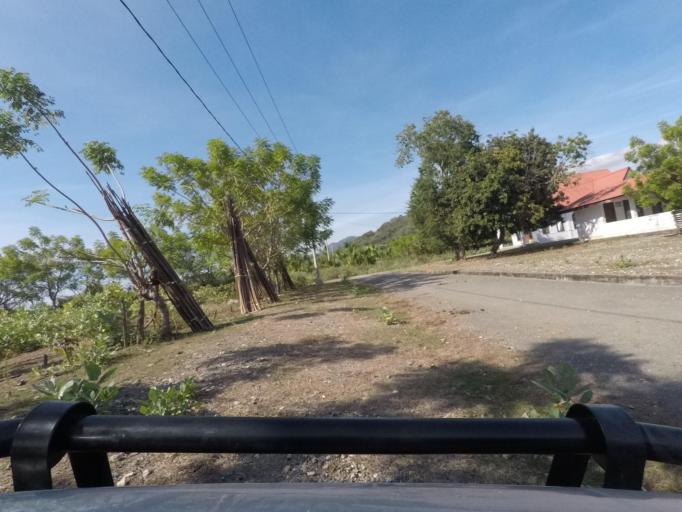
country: ID
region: East Nusa Tenggara
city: Atambua
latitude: -8.9576
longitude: 124.9621
